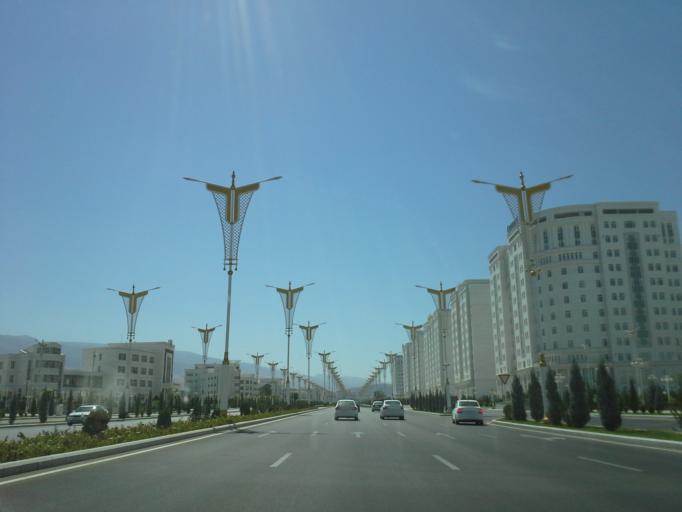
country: TM
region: Ahal
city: Ashgabat
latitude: 37.9151
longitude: 58.3636
